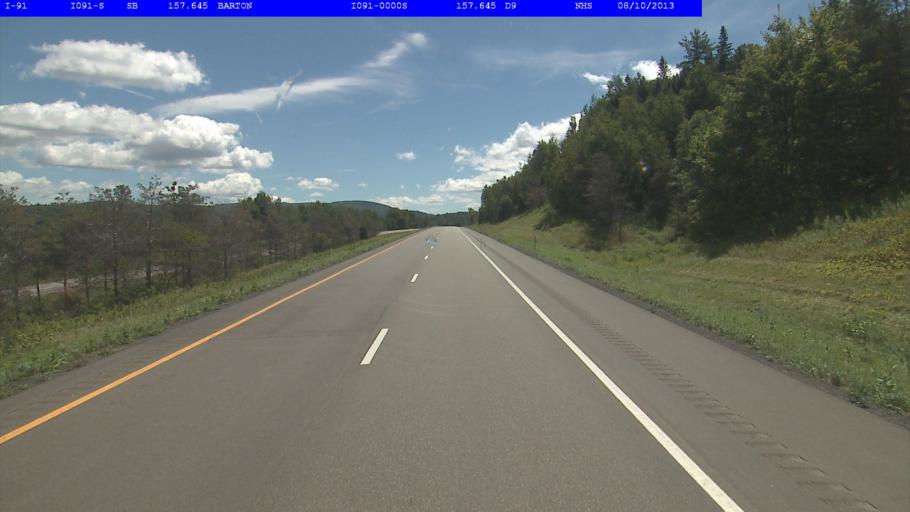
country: US
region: Vermont
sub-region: Orleans County
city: Newport
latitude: 44.7559
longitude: -72.2000
